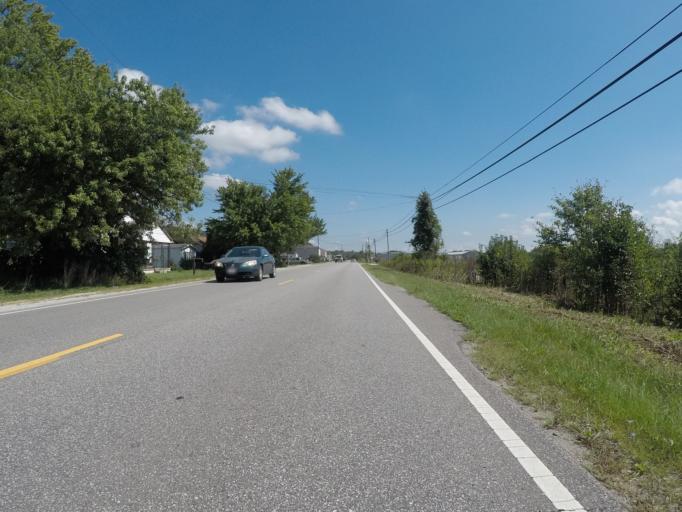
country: US
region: Ohio
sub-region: Lawrence County
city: Burlington
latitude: 38.4201
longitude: -82.4982
